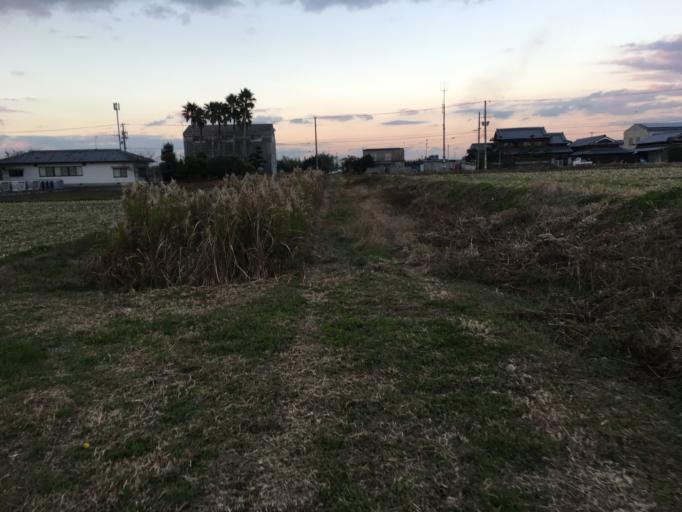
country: JP
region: Hyogo
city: Miki
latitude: 34.7368
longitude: 134.9504
